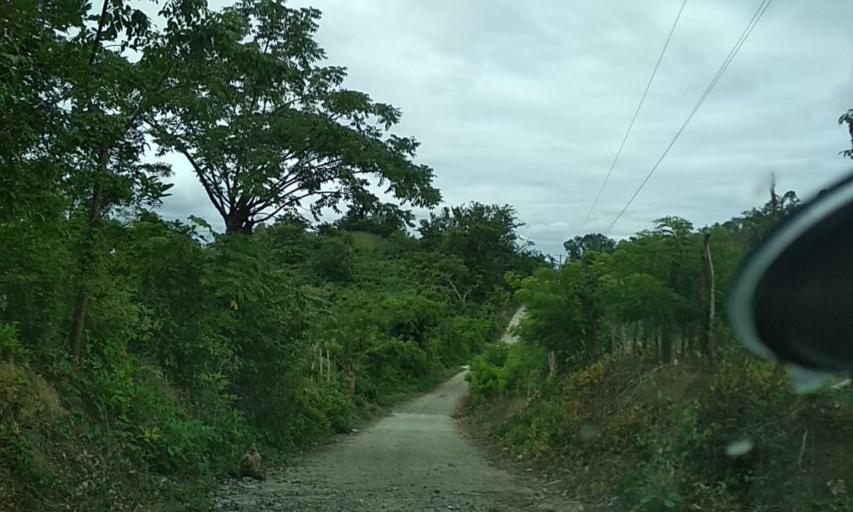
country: MX
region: Veracruz
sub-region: Papantla
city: Residencial Tajin
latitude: 20.6111
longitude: -97.3537
